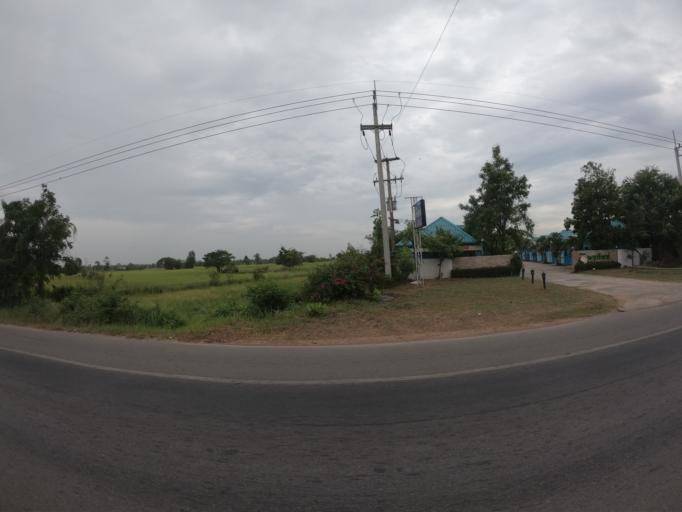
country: TH
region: Roi Et
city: Chiang Khwan
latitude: 16.1083
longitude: 103.8271
